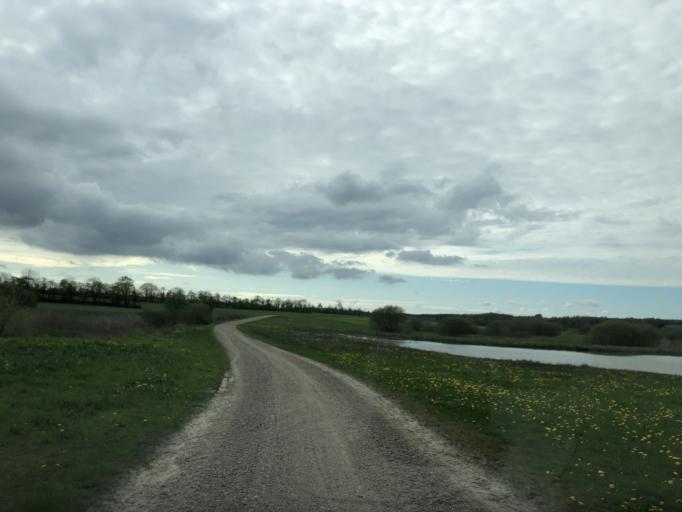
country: DK
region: Central Jutland
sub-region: Holstebro Kommune
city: Ulfborg
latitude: 56.1945
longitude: 8.4645
